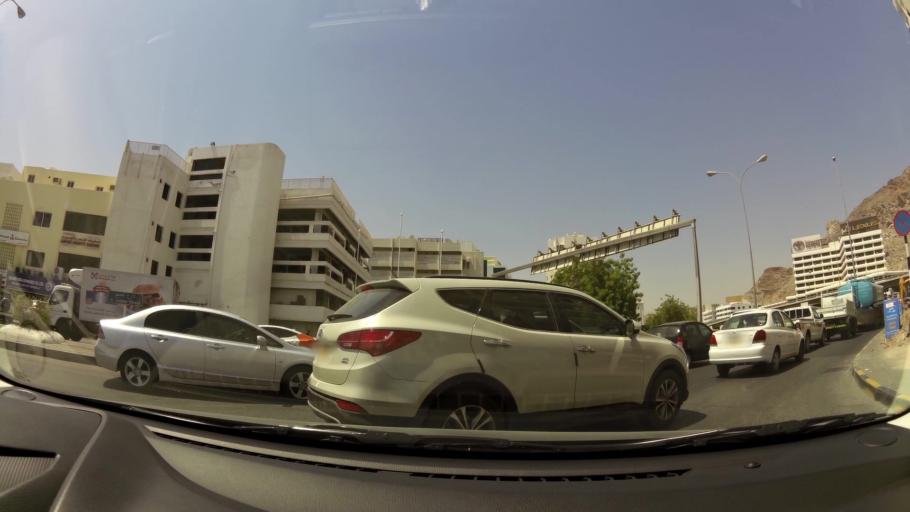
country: OM
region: Muhafazat Masqat
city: Muscat
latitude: 23.5944
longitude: 58.5439
